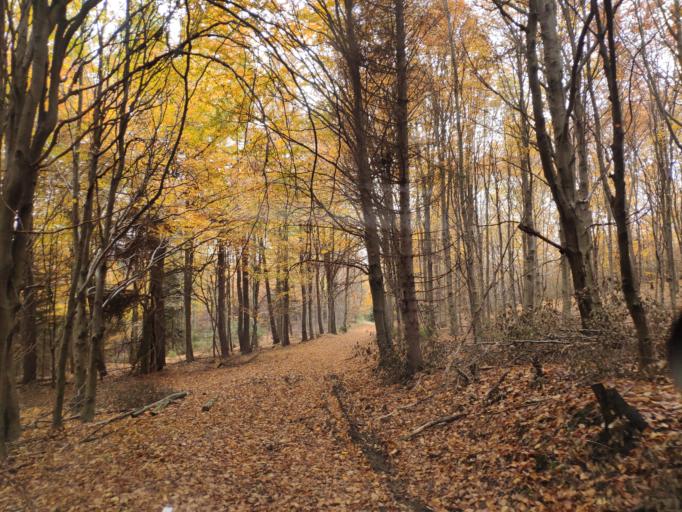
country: SK
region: Kosicky
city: Medzev
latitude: 48.7420
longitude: 20.9916
